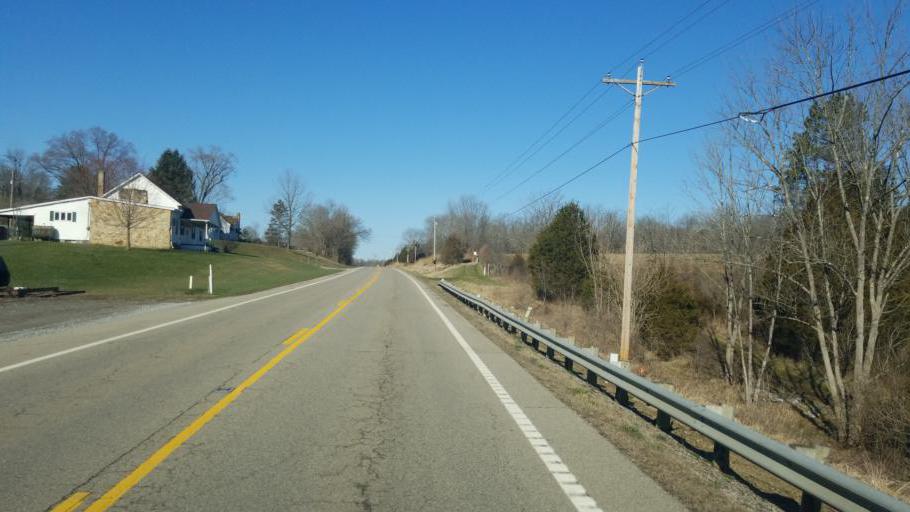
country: US
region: Ohio
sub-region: Highland County
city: Greenfield
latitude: 39.2310
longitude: -83.3329
